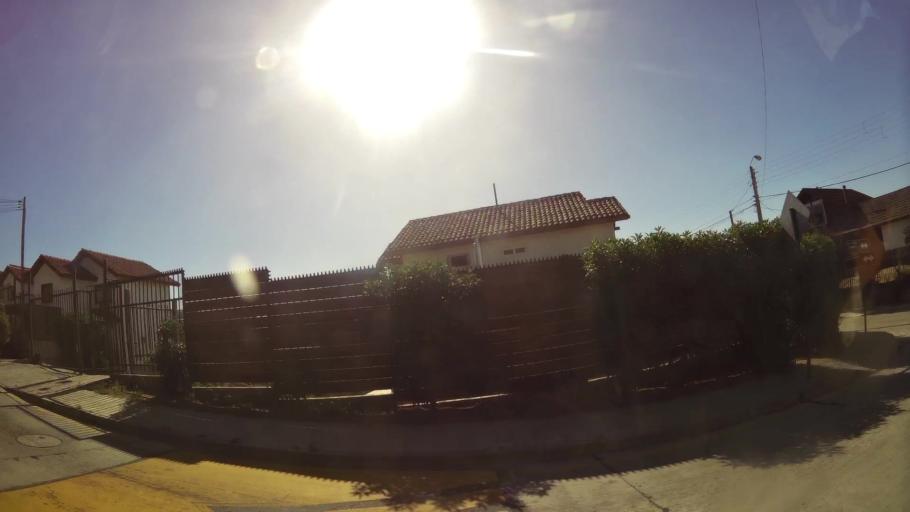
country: CL
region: Valparaiso
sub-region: Provincia de Valparaiso
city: Vina del Mar
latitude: -33.0375
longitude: -71.5564
